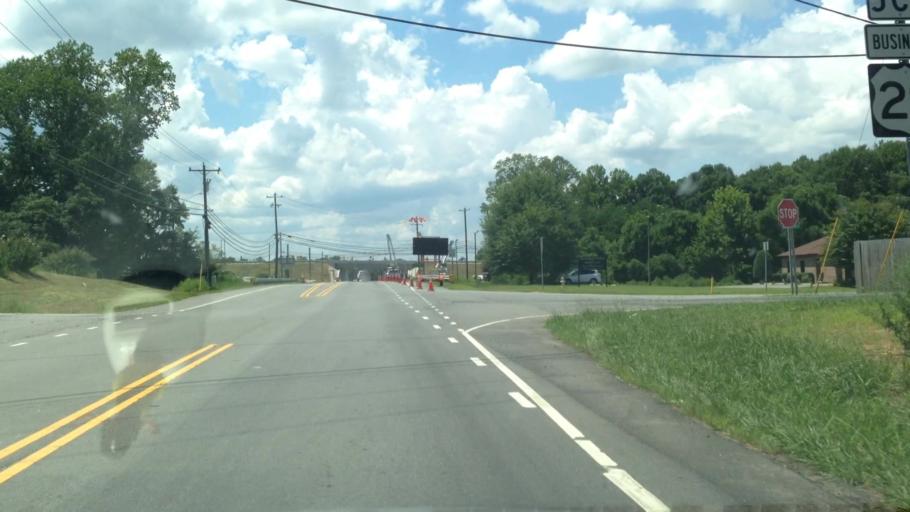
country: US
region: North Carolina
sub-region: Rockingham County
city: Reidsville
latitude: 36.3570
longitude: -79.6856
